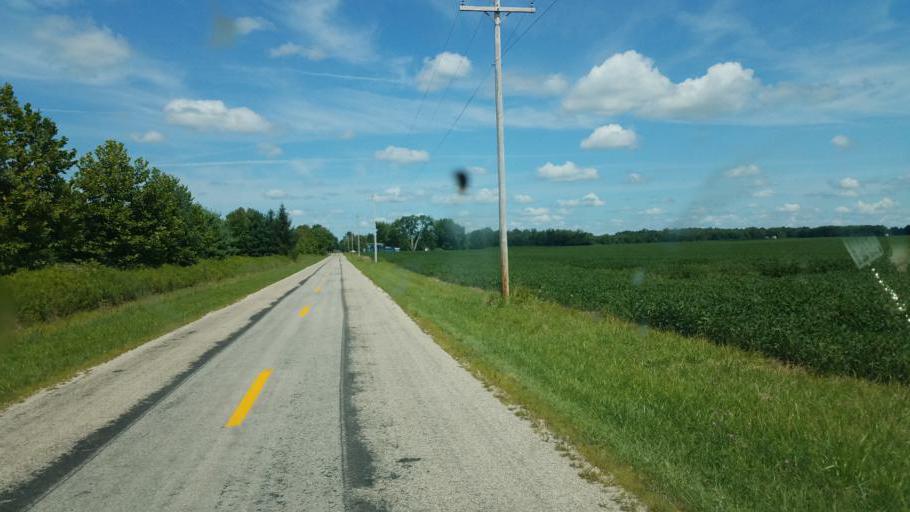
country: US
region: Ohio
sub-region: Delaware County
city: Sunbury
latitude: 40.2992
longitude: -82.8063
